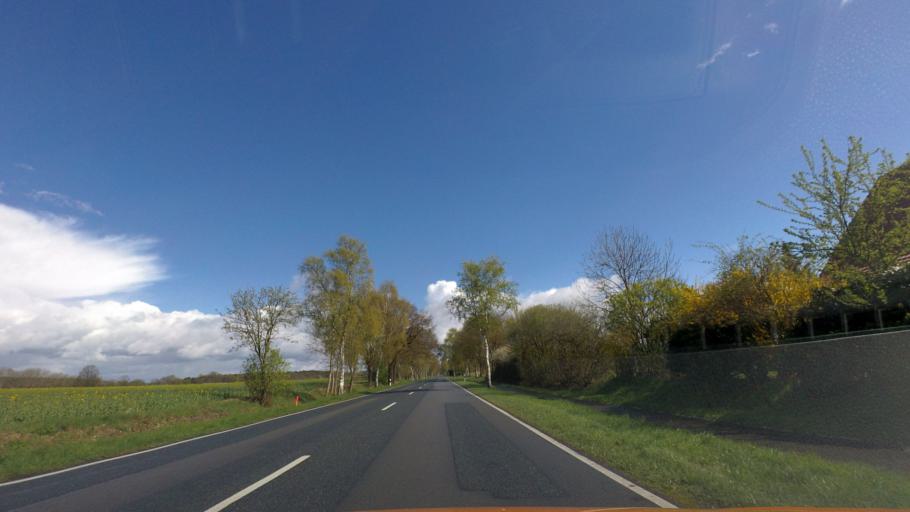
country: DE
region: Lower Saxony
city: Ottersberg
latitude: 53.0746
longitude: 9.1008
